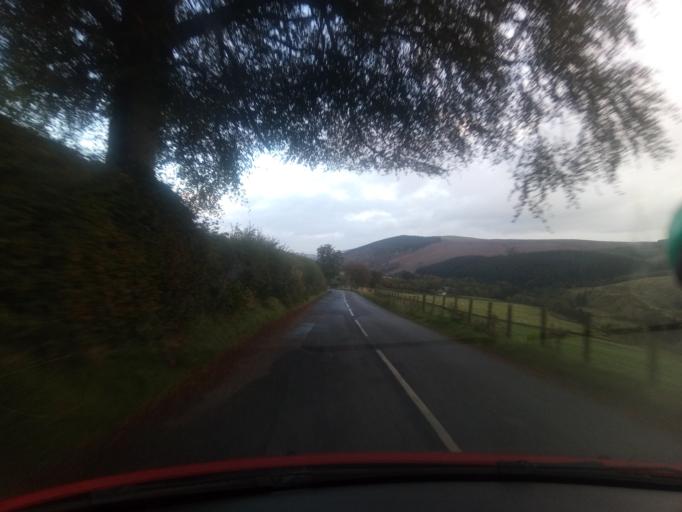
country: GB
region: Scotland
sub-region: The Scottish Borders
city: Hawick
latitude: 55.3404
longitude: -2.6517
